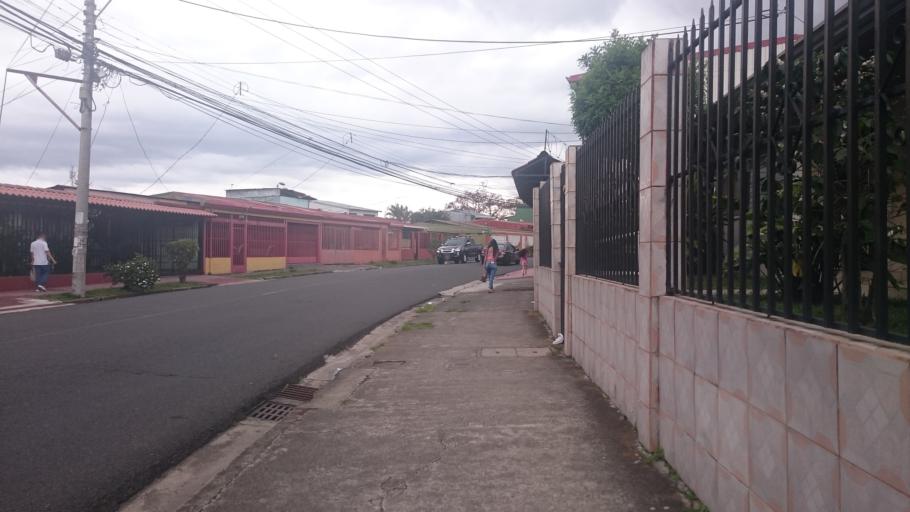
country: CR
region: San Jose
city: San Felipe
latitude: 9.9169
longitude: -84.1039
